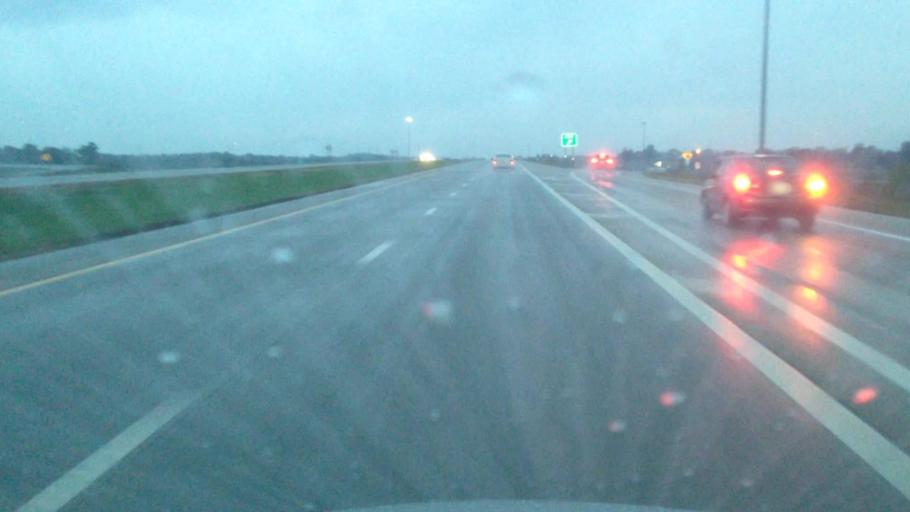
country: US
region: Kansas
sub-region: Douglas County
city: Baldwin City
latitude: 38.7858
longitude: -95.2692
